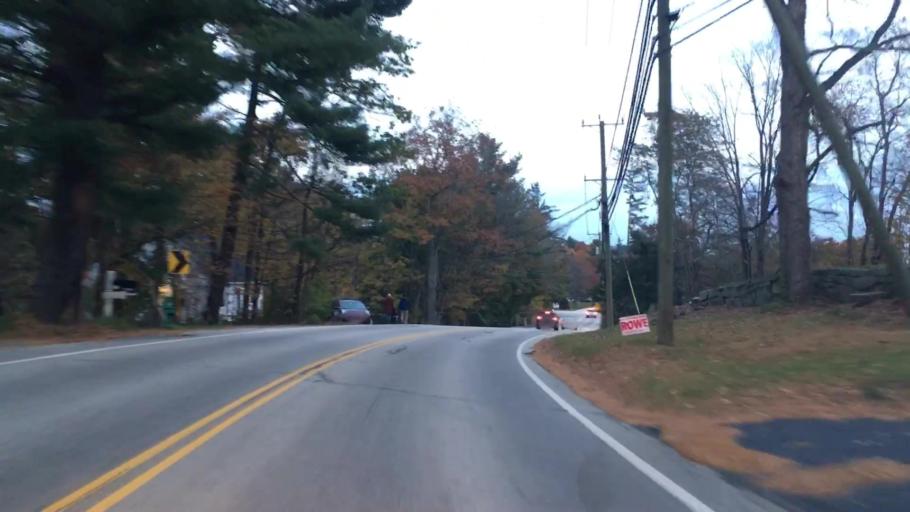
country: US
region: New Hampshire
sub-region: Hillsborough County
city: Milford
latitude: 42.8606
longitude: -71.6325
